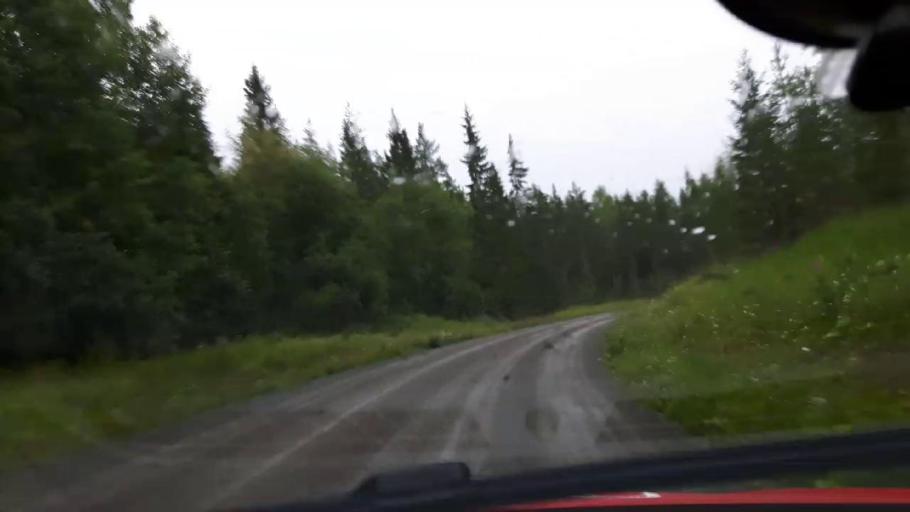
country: SE
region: Jaemtland
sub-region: OEstersunds Kommun
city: Brunflo
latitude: 62.9785
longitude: 14.8300
